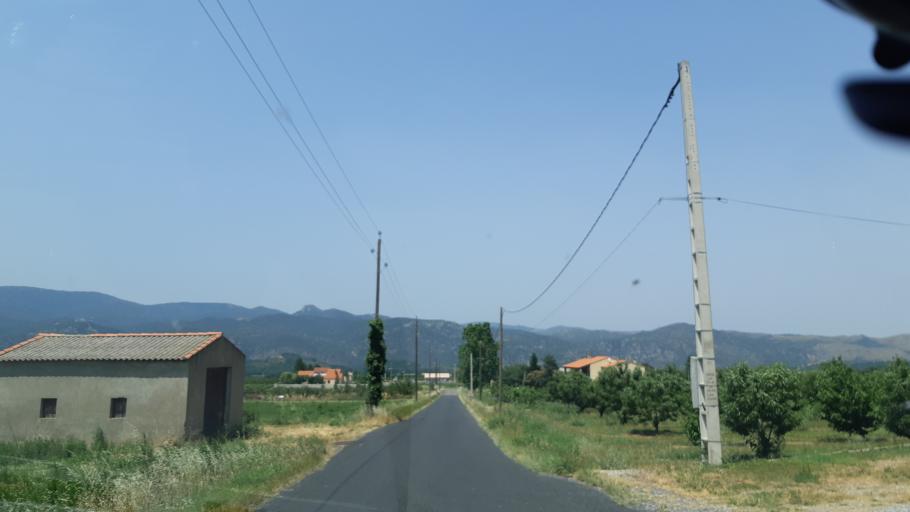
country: FR
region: Languedoc-Roussillon
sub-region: Departement des Pyrenees-Orientales
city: Vinca
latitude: 42.6191
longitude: 2.5188
